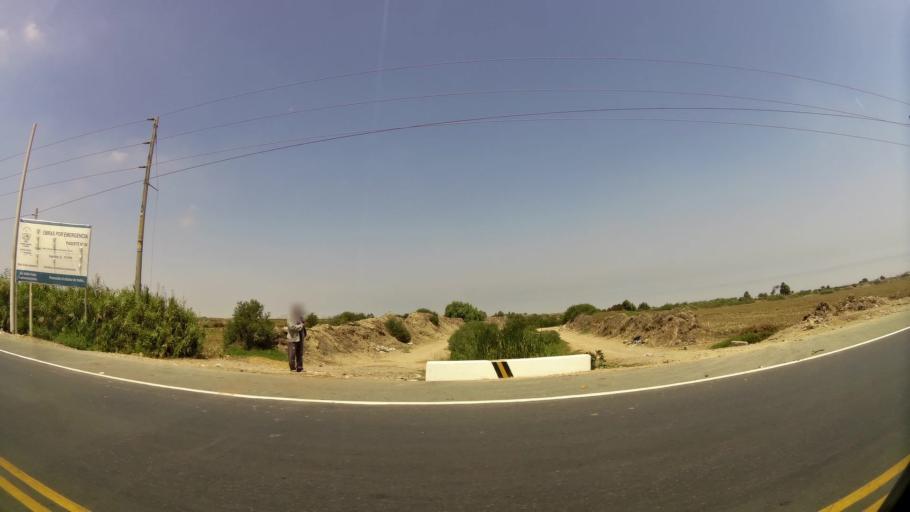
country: PE
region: La Libertad
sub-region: Provincia de Pacasmayo
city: Pacasmayo
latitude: -7.4198
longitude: -79.5436
